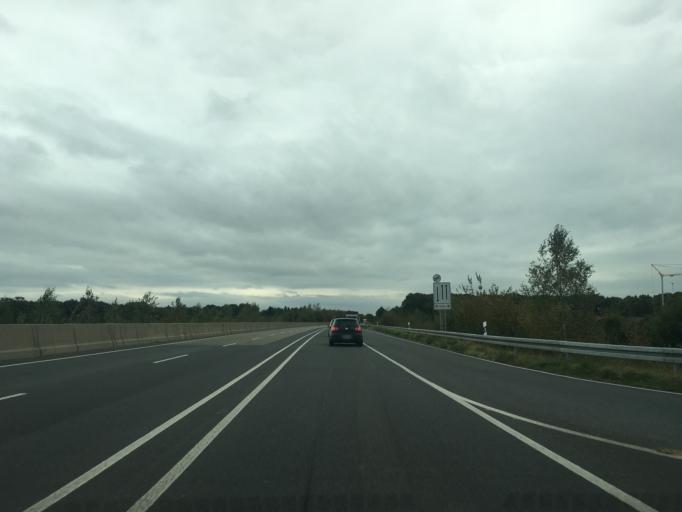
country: DE
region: North Rhine-Westphalia
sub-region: Regierungsbezirk Munster
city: Ochtrup
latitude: 52.1904
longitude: 7.2184
